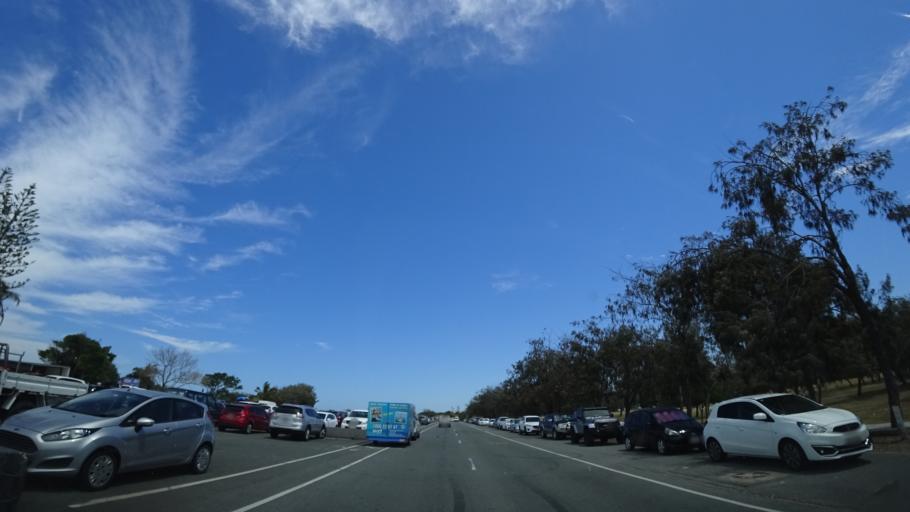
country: AU
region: Queensland
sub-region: Gold Coast
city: Southport
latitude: -27.9379
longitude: 153.4260
